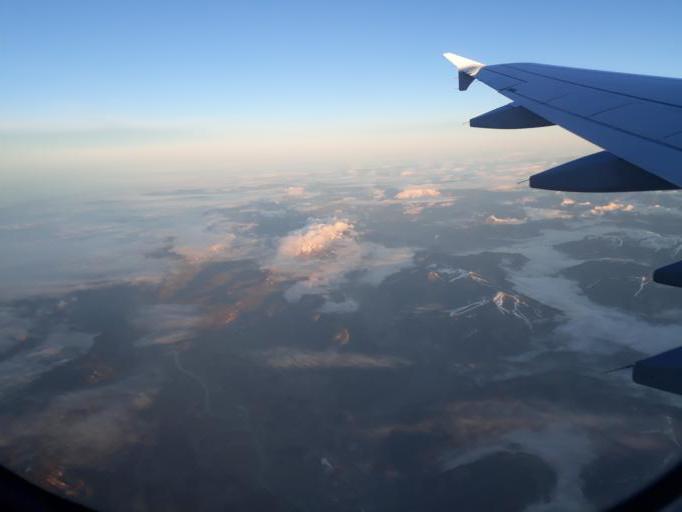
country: AT
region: Tyrol
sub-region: Politischer Bezirk Kufstein
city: Radfeld
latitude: 47.4575
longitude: 11.9401
